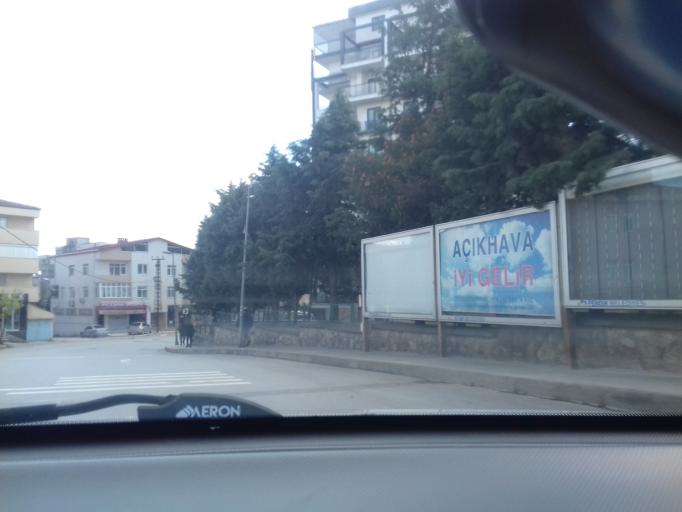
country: TR
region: Istanbul
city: Pendik
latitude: 40.8926
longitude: 29.2765
